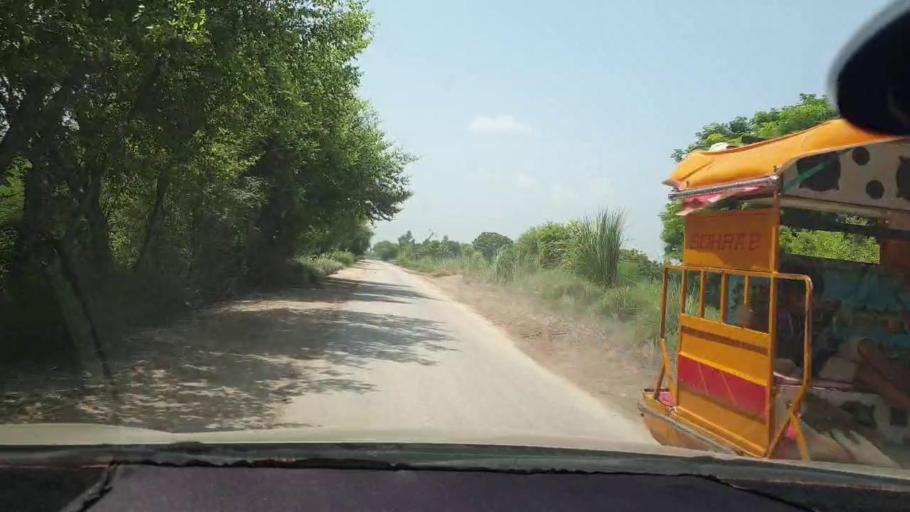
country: PK
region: Sindh
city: Kambar
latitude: 27.6629
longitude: 67.9302
